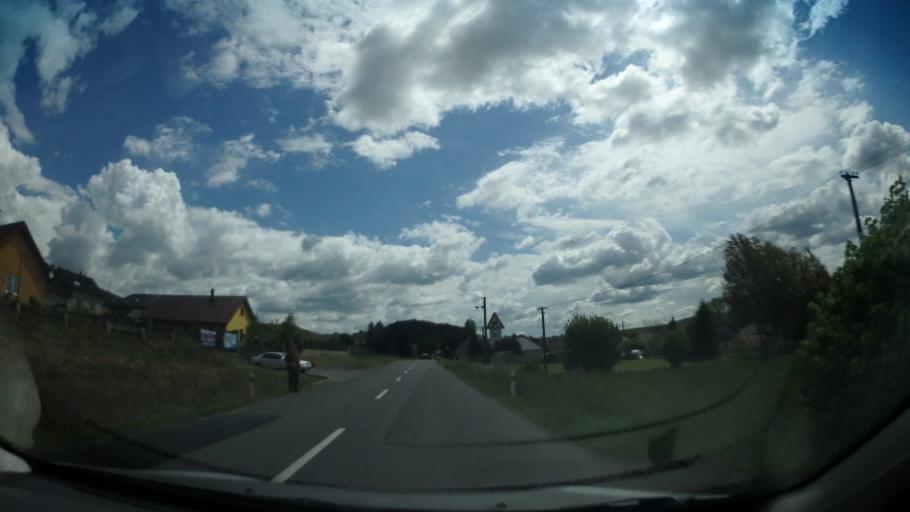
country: CZ
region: Pardubicky
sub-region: Okres Svitavy
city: Moravska Trebova
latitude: 49.7345
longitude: 16.6439
